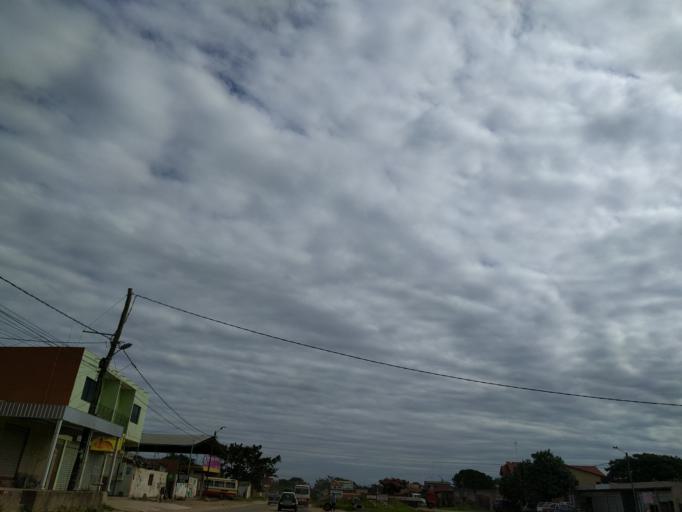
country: BO
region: Santa Cruz
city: Santa Cruz de la Sierra
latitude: -17.8298
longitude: -63.2395
